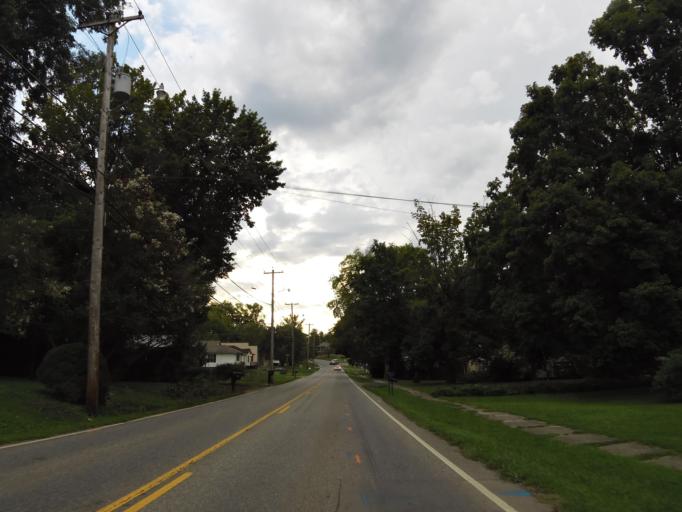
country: US
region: Tennessee
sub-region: Blount County
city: Maryville
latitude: 35.7591
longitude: -83.9603
